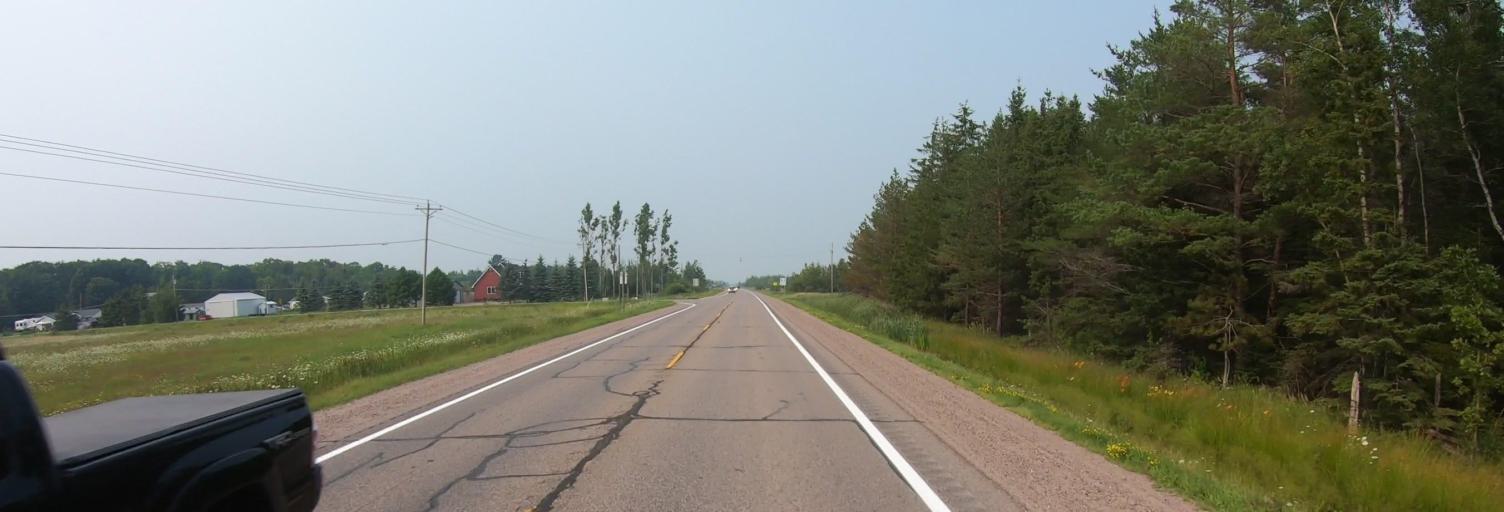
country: US
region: Michigan
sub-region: Chippewa County
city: Sault Ste. Marie
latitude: 46.4186
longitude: -84.3535
